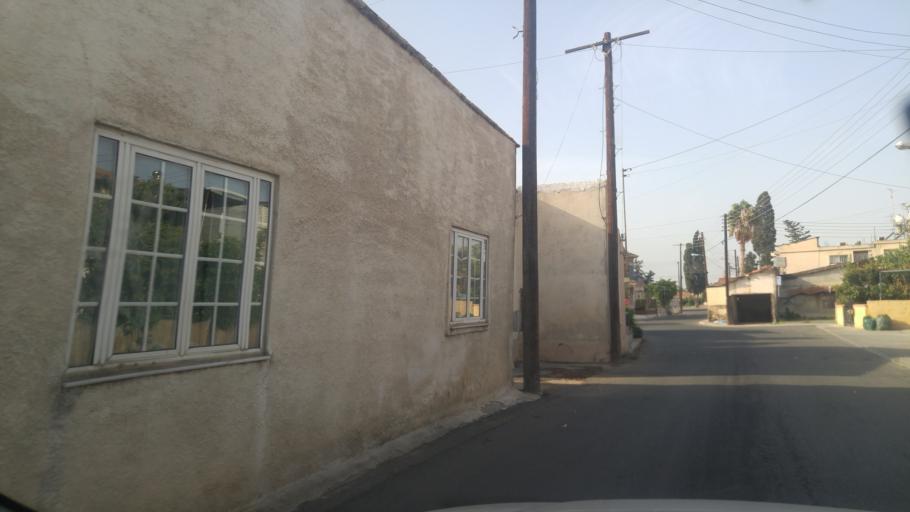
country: CY
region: Limassol
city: Limassol
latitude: 34.6602
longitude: 33.0028
